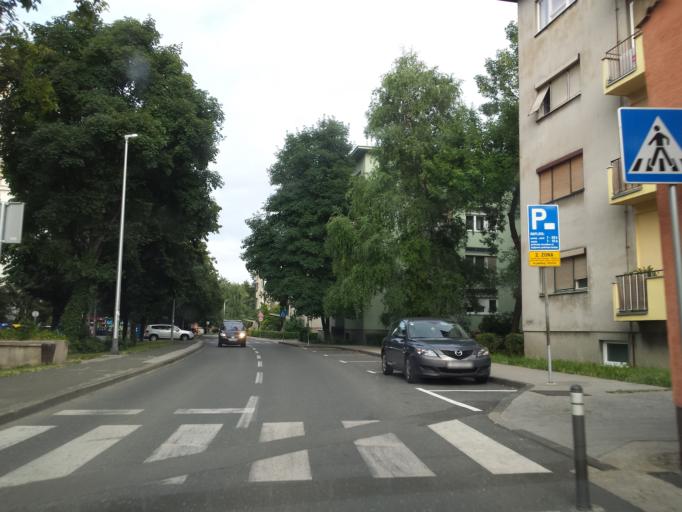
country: HR
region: Grad Zagreb
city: Novi Zagreb
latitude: 45.7994
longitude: 16.0001
